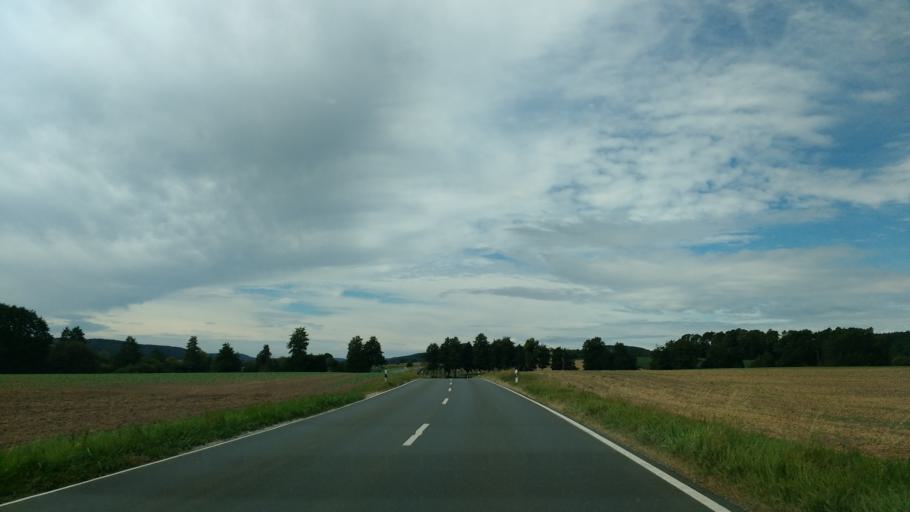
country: DE
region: Bavaria
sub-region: Upper Franconia
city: Schlusselfeld
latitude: 49.7628
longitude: 10.6016
